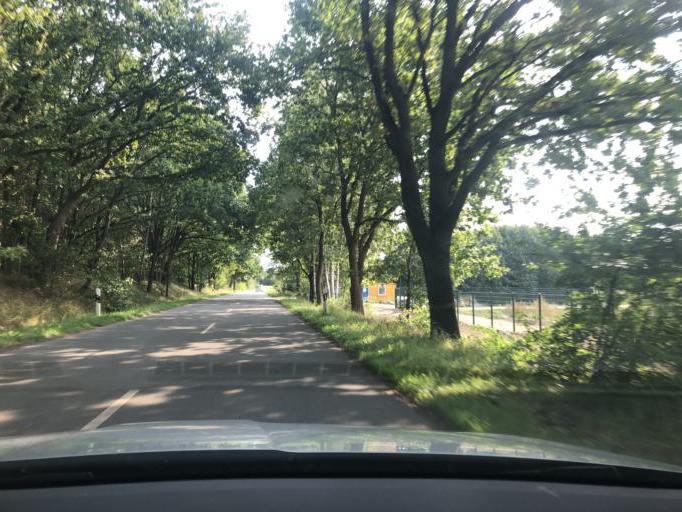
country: DE
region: Schleswig-Holstein
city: Gross Gronau
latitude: 53.8021
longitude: 10.7304
